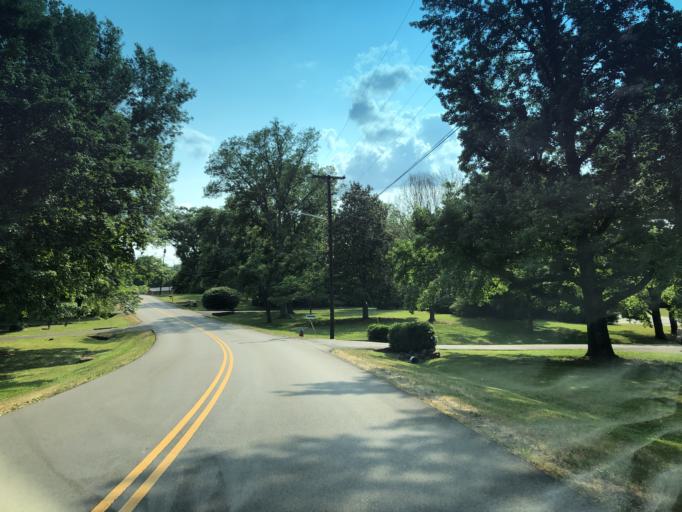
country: US
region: Tennessee
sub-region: Davidson County
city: Goodlettsville
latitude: 36.2737
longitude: -86.7229
